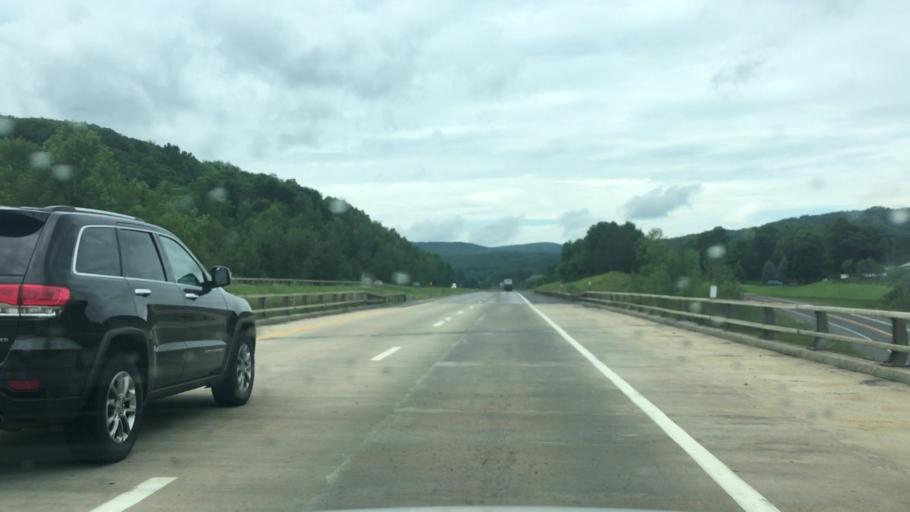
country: US
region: New York
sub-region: Schoharie County
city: Cobleskill
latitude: 42.6449
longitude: -74.5892
